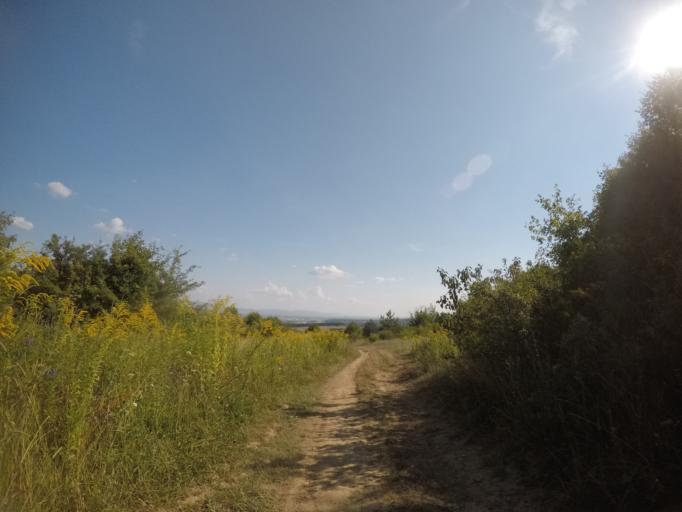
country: SK
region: Kosicky
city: Kosice
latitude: 48.7409
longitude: 21.2086
